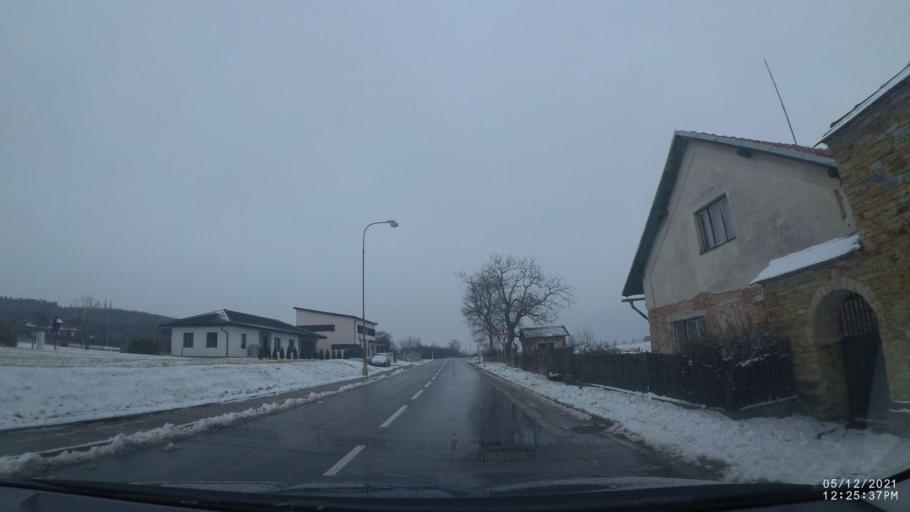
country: CZ
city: Ceske Mezirici
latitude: 50.3236
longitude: 16.0905
